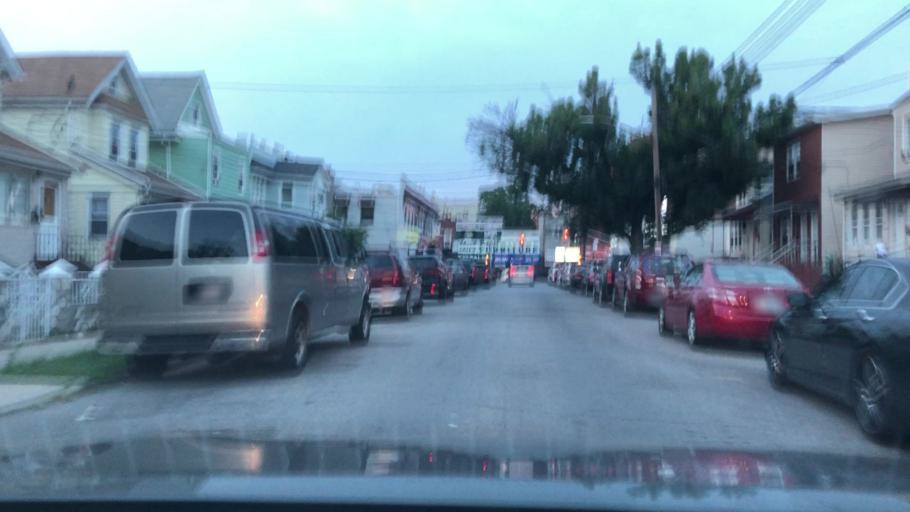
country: US
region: New York
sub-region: Queens County
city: Borough of Queens
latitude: 40.6865
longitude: -73.8213
